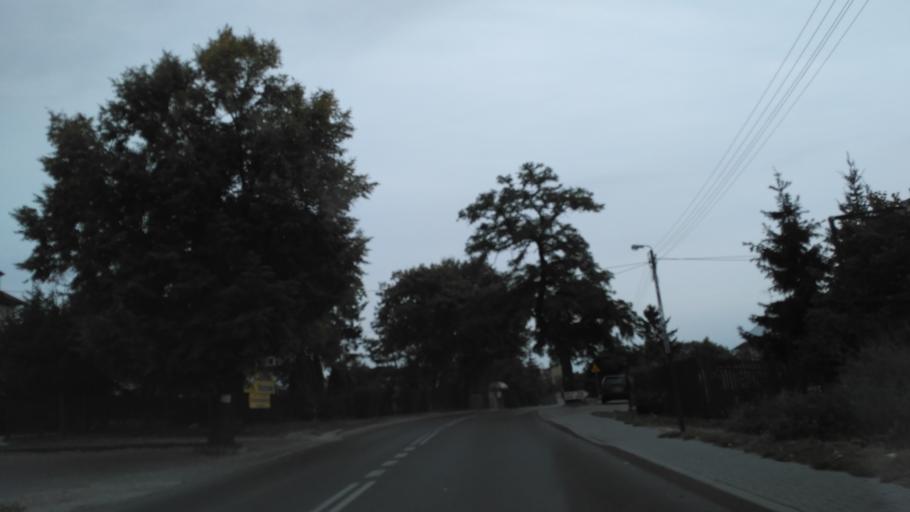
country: PL
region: Lublin Voivodeship
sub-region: Powiat lubelski
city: Lublin
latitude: 51.2219
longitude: 22.5885
